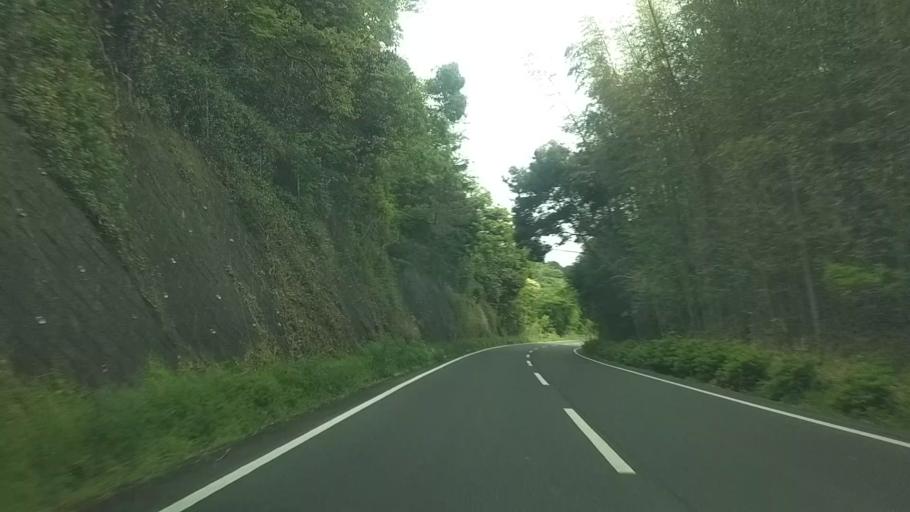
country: JP
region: Shizuoka
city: Kosai-shi
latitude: 34.7463
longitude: 137.5990
